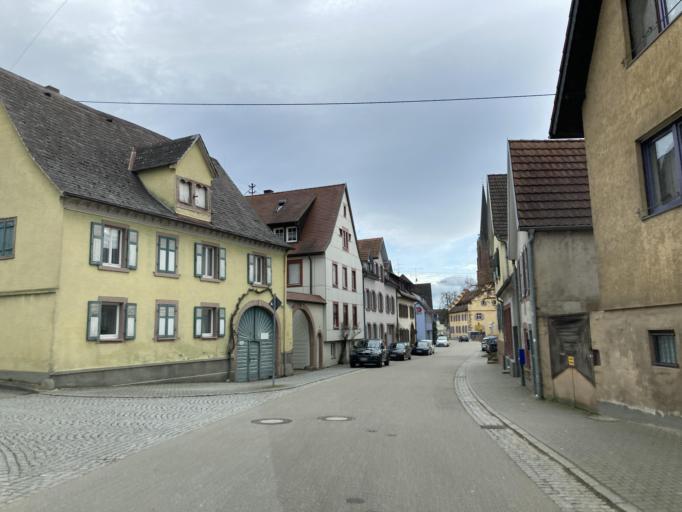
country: DE
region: Baden-Wuerttemberg
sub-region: Freiburg Region
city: Eichstetten
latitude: 48.0946
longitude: 7.7433
